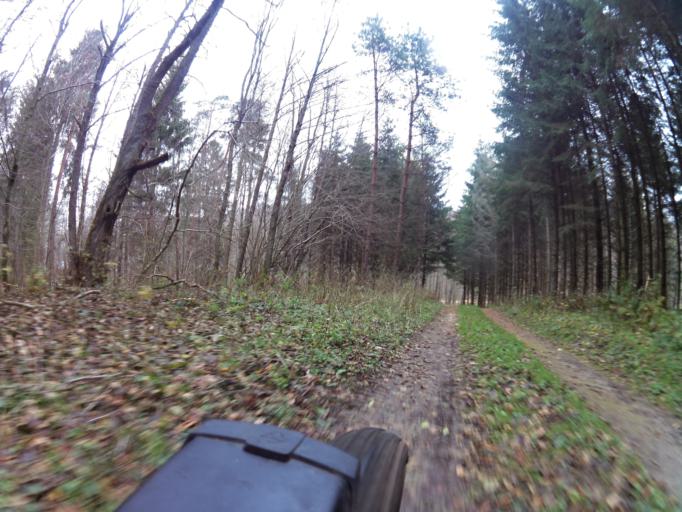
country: PL
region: West Pomeranian Voivodeship
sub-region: Powiat koszalinski
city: Polanow
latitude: 54.0572
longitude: 16.6729
